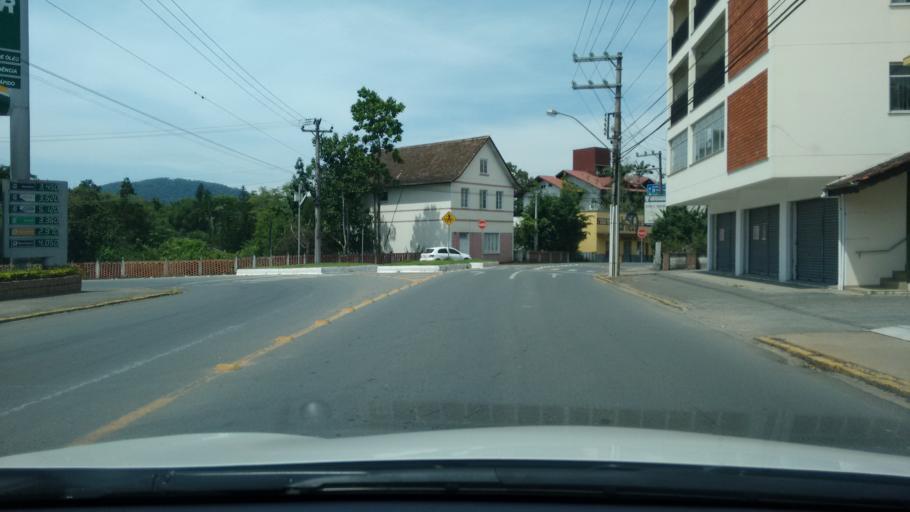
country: BR
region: Santa Catarina
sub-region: Timbo
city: Timbo
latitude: -26.8286
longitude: -49.2756
